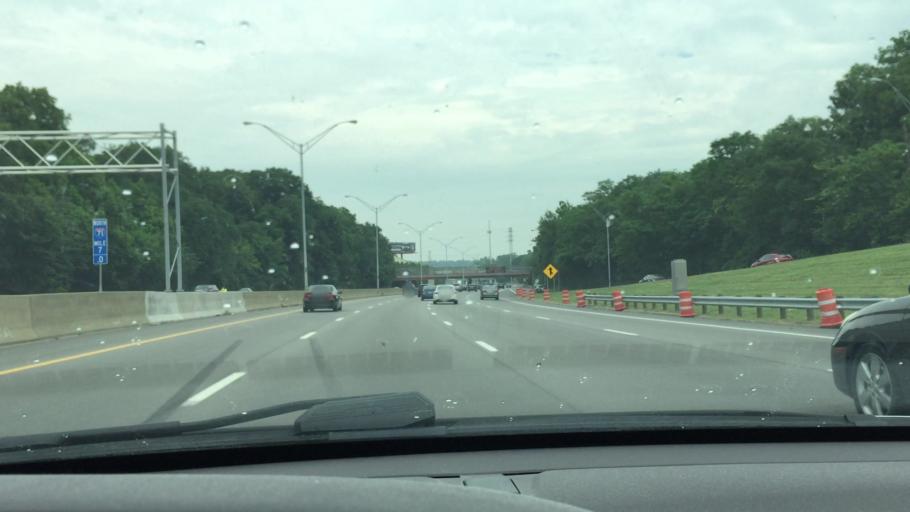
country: US
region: Ohio
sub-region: Hamilton County
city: Cincinnati
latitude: 39.1536
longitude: -84.4424
